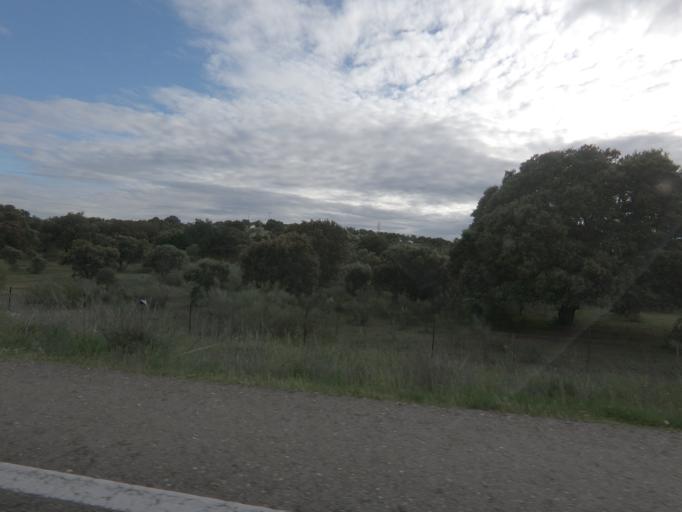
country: ES
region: Extremadura
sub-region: Provincia de Caceres
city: Torrejoncillo
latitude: 39.9089
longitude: -6.4798
